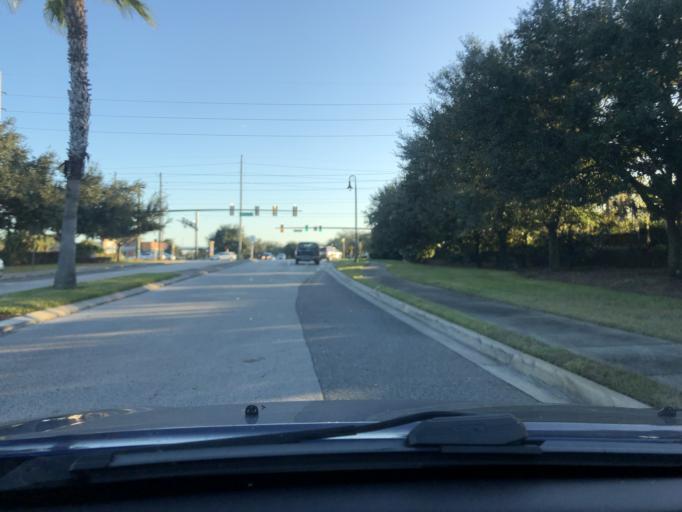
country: US
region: Florida
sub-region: Seminole County
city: Goldenrod
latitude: 28.6195
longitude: -81.2618
